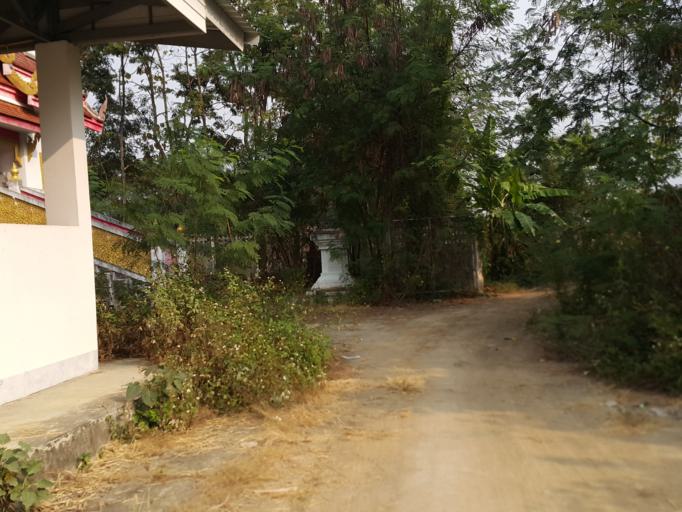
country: TH
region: Chiang Mai
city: San Kamphaeng
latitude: 18.7754
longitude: 99.0918
